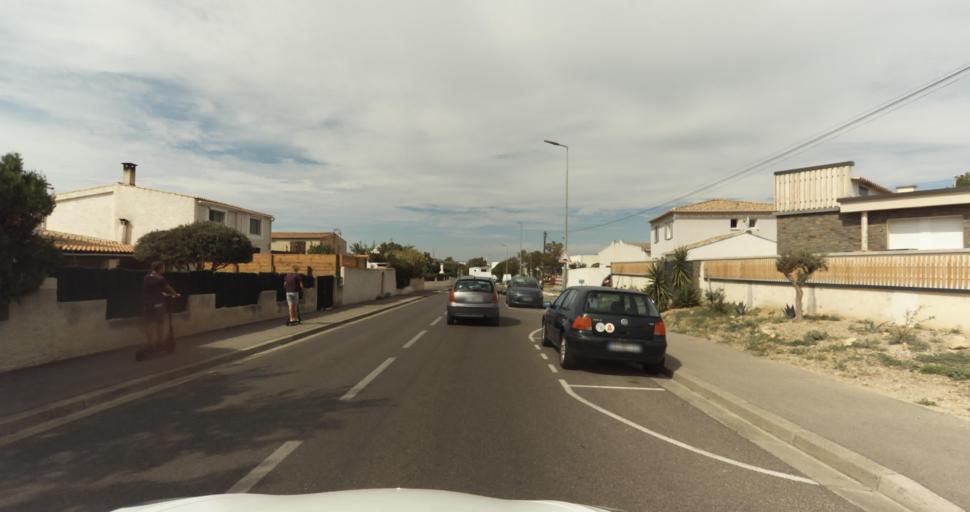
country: FR
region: Provence-Alpes-Cote d'Azur
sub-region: Departement des Bouches-du-Rhone
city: Miramas
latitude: 43.5759
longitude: 5.0076
